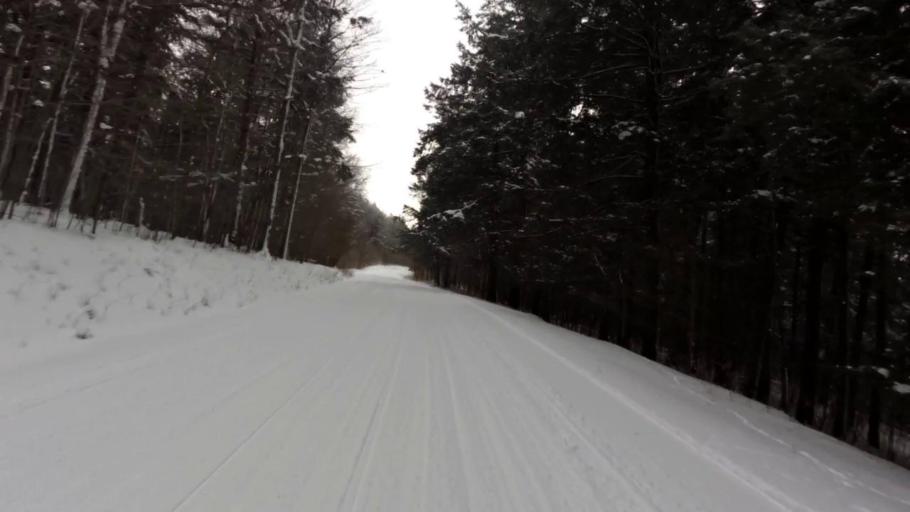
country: US
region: New York
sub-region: Cattaraugus County
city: Salamanca
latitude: 42.0588
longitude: -78.7625
